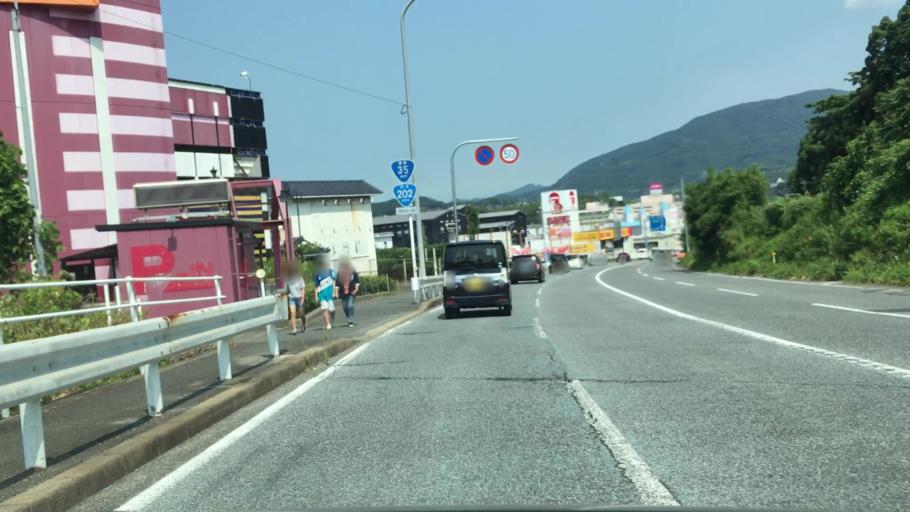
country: JP
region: Nagasaki
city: Sasebo
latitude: 33.1427
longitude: 129.7877
